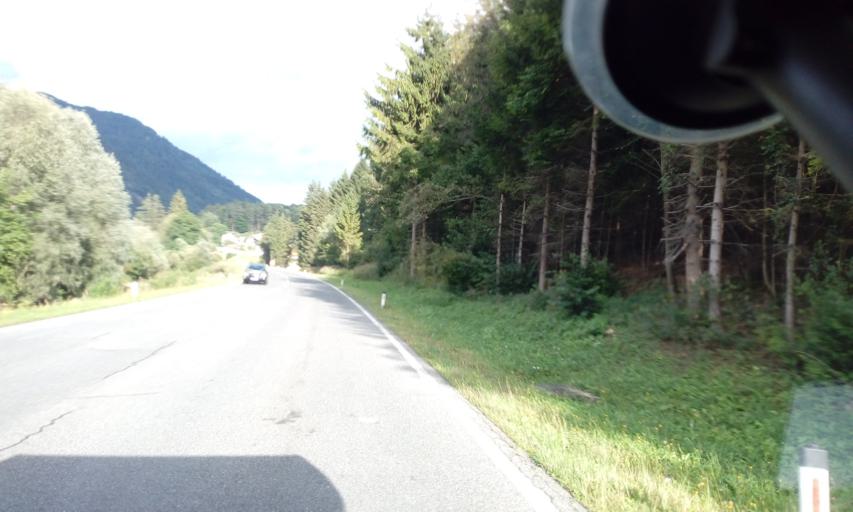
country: AT
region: Carinthia
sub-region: Villach Stadt
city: Villach
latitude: 46.6488
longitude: 13.7748
